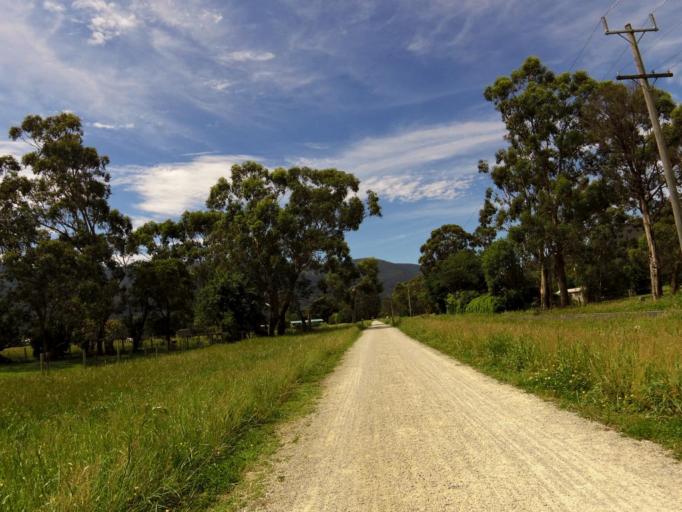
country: AU
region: Victoria
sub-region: Yarra Ranges
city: Millgrove
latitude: -37.7681
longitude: 145.6346
